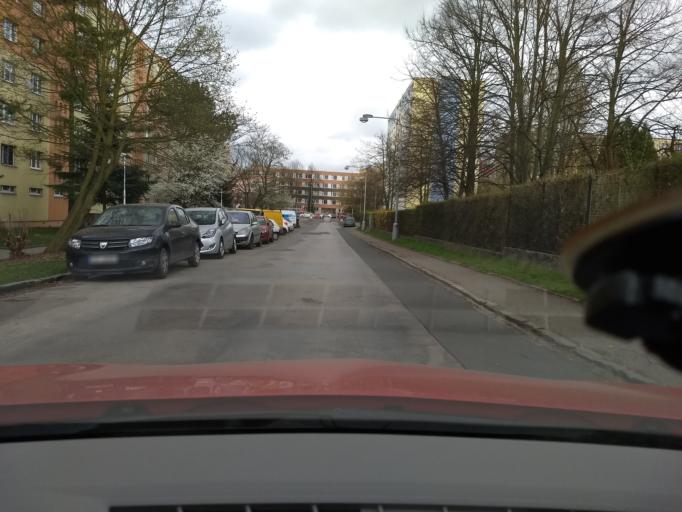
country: CZ
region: Central Bohemia
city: Kladno
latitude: 50.1310
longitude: 14.1214
